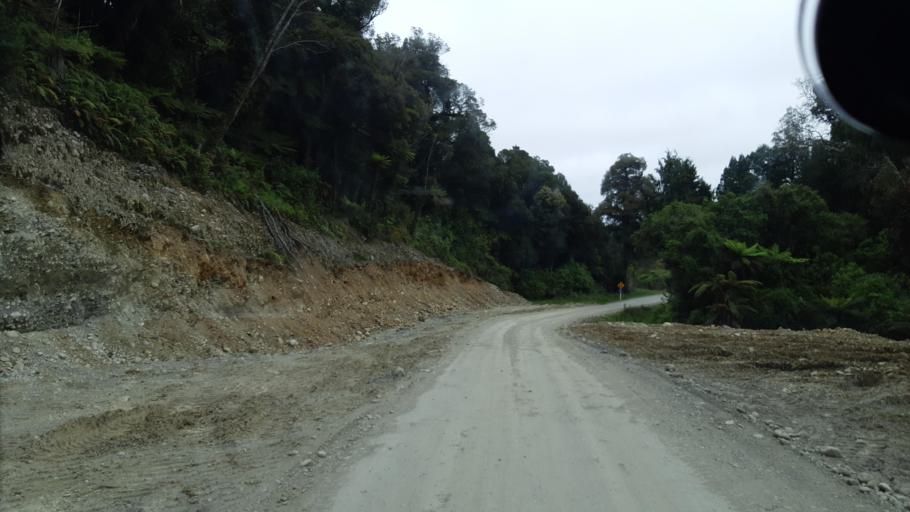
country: NZ
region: West Coast
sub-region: Grey District
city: Greymouth
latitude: -42.6409
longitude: 171.2950
